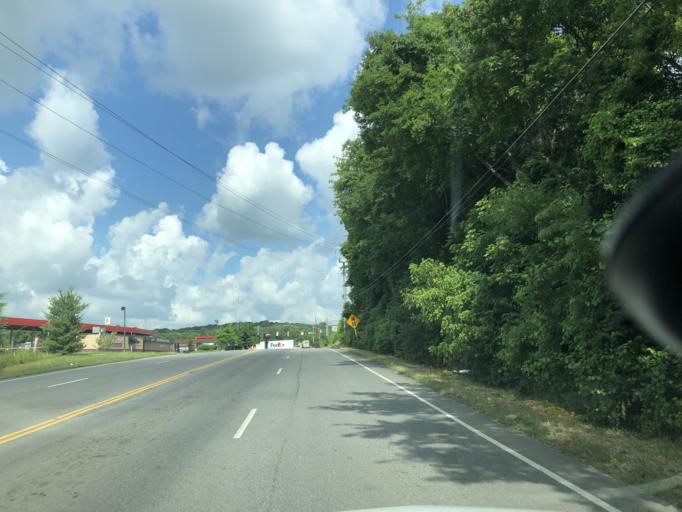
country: US
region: Tennessee
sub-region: Rutherford County
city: La Vergne
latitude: 36.0167
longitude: -86.6178
